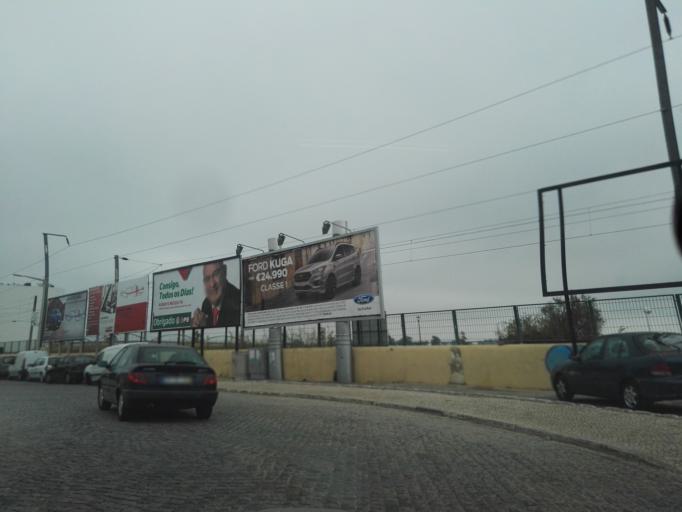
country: PT
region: Lisbon
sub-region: Vila Franca de Xira
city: Vila Franca de Xira
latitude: 38.9507
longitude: -8.9903
